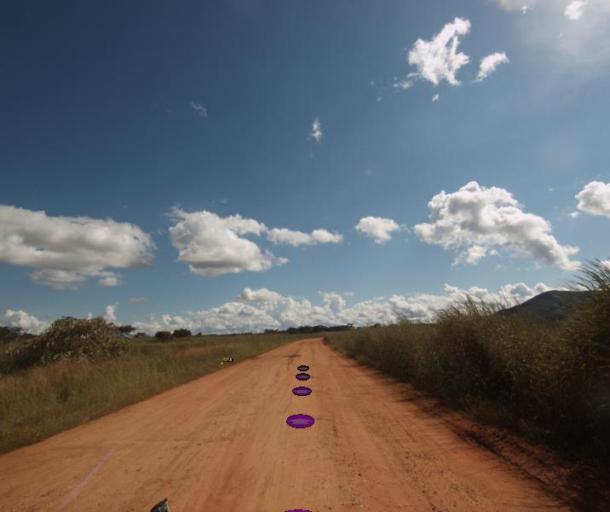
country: BR
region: Goias
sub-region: Jaragua
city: Jaragua
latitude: -15.8335
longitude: -49.2638
